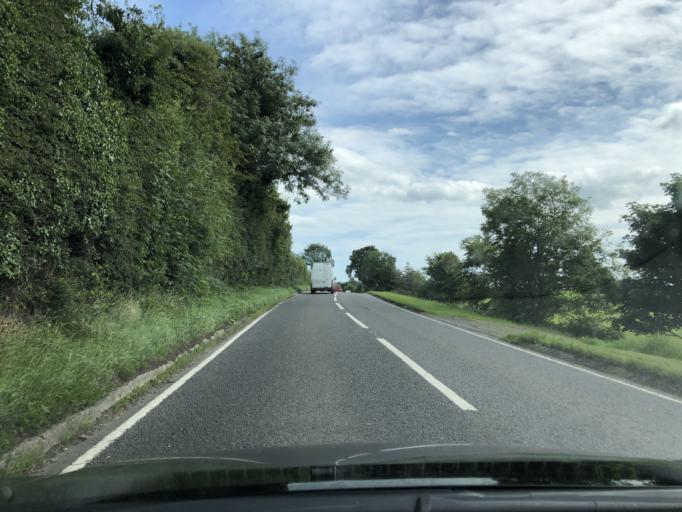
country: GB
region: Northern Ireland
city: Ballynahinch
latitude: 54.4256
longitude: -5.9230
